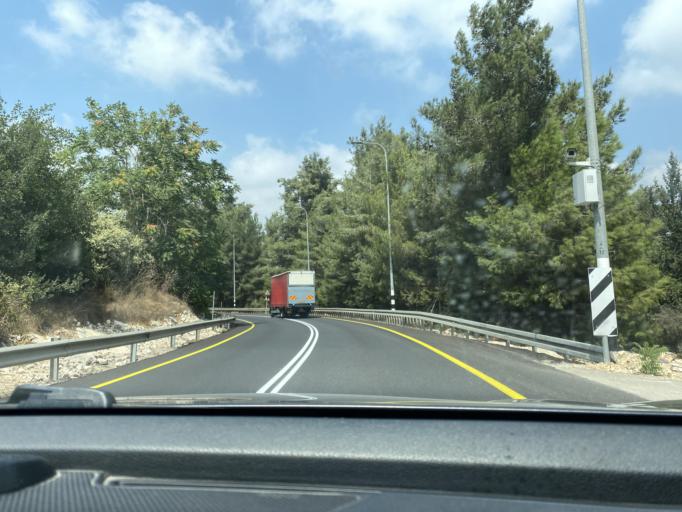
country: IL
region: Northern District
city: Kefar Weradim
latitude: 33.0036
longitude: 35.2841
